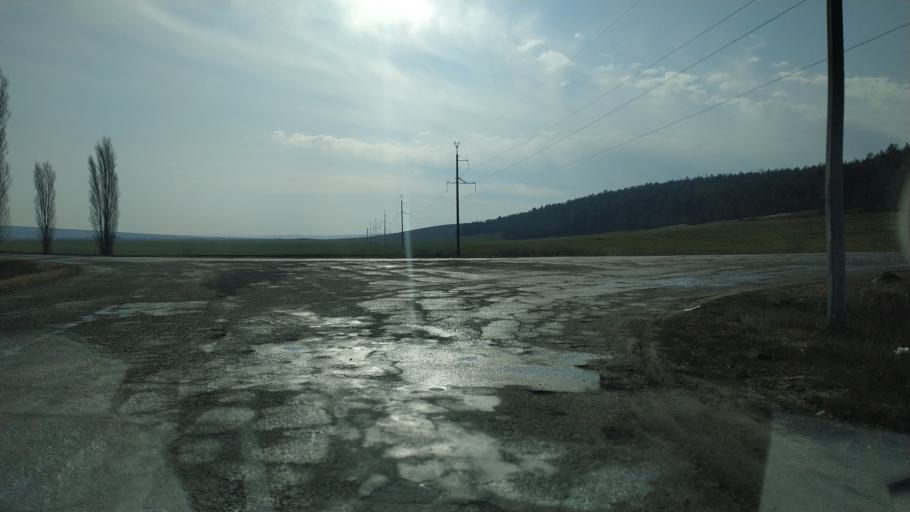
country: MD
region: Chisinau
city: Singera
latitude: 46.6977
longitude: 29.0668
